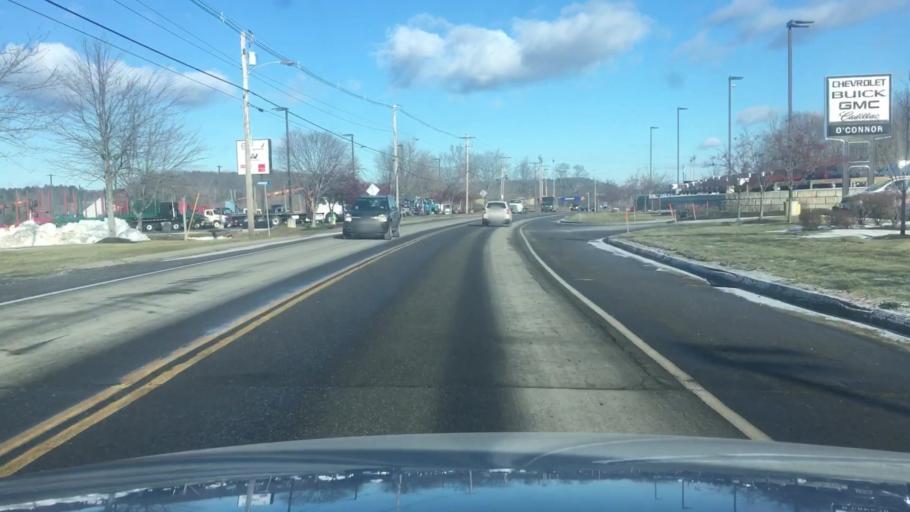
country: US
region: Maine
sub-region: Kennebec County
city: Augusta
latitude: 44.3298
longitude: -69.7626
